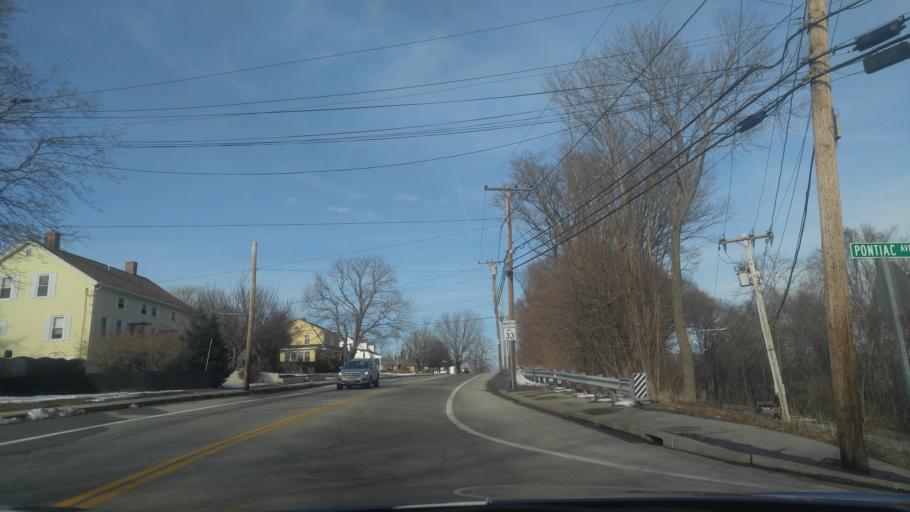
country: US
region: Rhode Island
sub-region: Kent County
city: West Warwick
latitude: 41.7258
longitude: -71.4914
